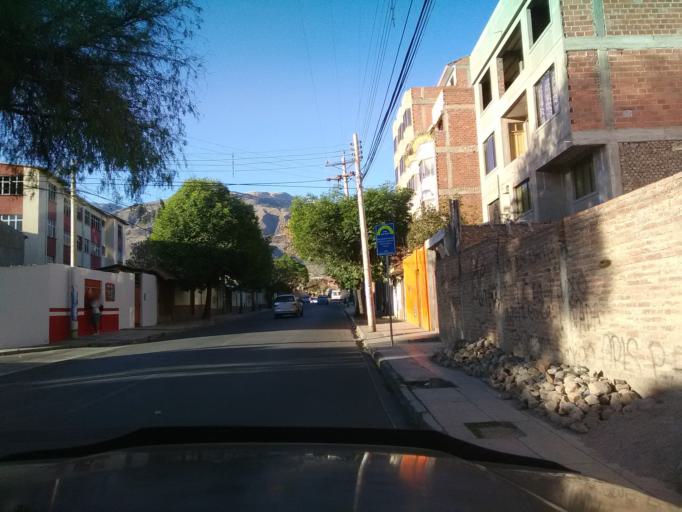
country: BO
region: Cochabamba
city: Cochabamba
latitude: -17.3600
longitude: -66.1839
